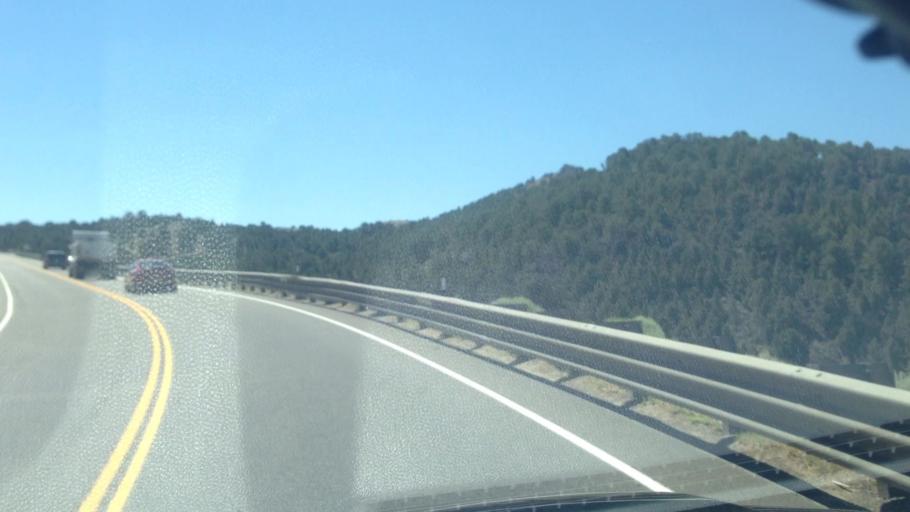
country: US
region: Nevada
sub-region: Storey County
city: Virginia City
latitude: 39.3521
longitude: -119.6593
